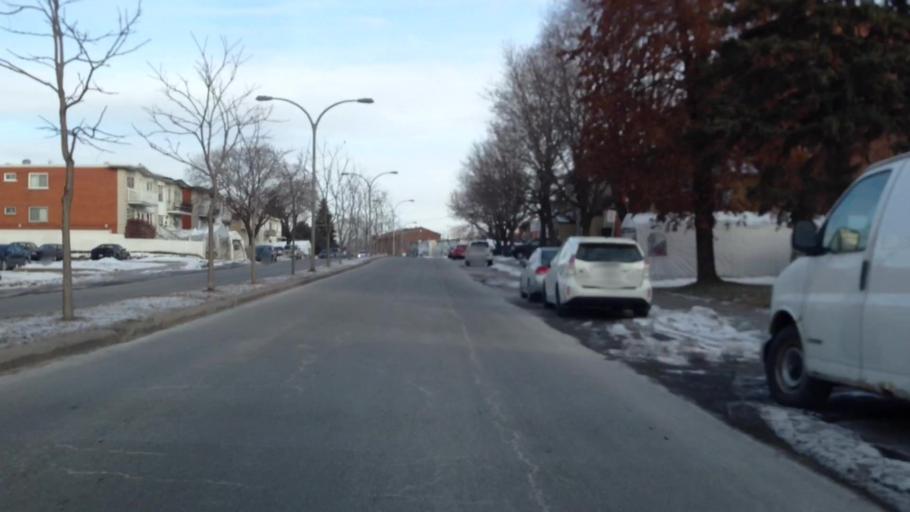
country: CA
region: Quebec
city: Dollard-Des Ormeaux
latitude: 45.5328
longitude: -73.7754
